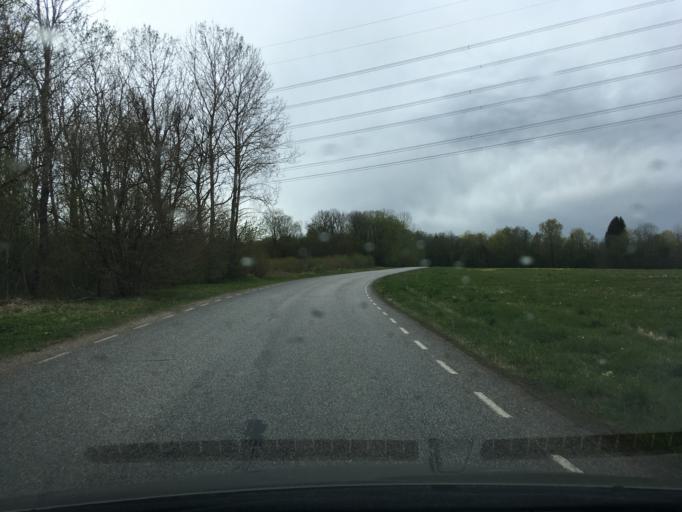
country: EE
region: Harju
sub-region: Rae vald
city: Vaida
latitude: 59.3039
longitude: 24.9865
